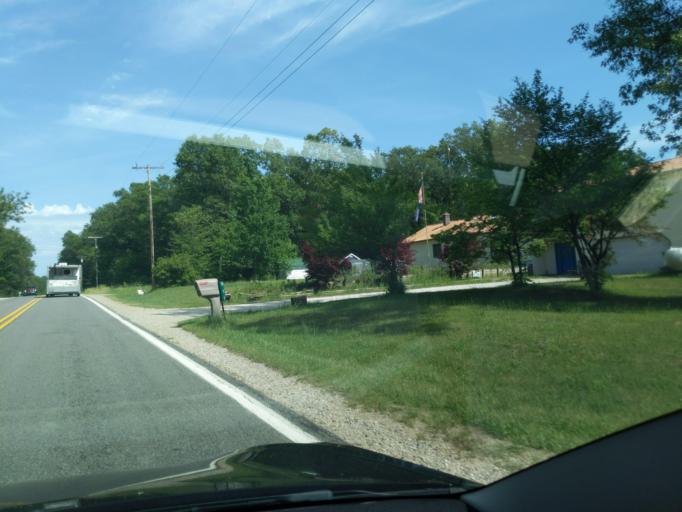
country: US
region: Michigan
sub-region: Muskegon County
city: Lakewood Club
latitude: 43.4064
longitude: -86.2643
